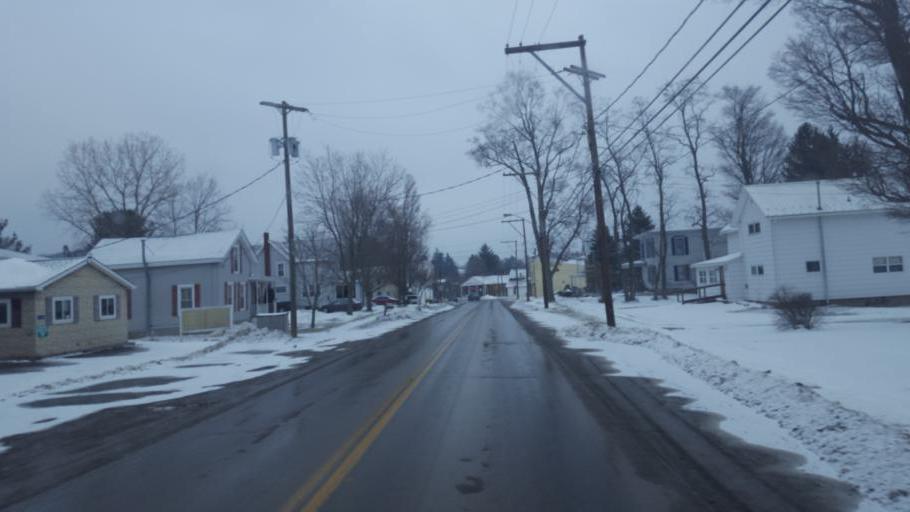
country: US
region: Pennsylvania
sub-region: Tioga County
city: Elkland
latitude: 42.0796
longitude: -77.4115
